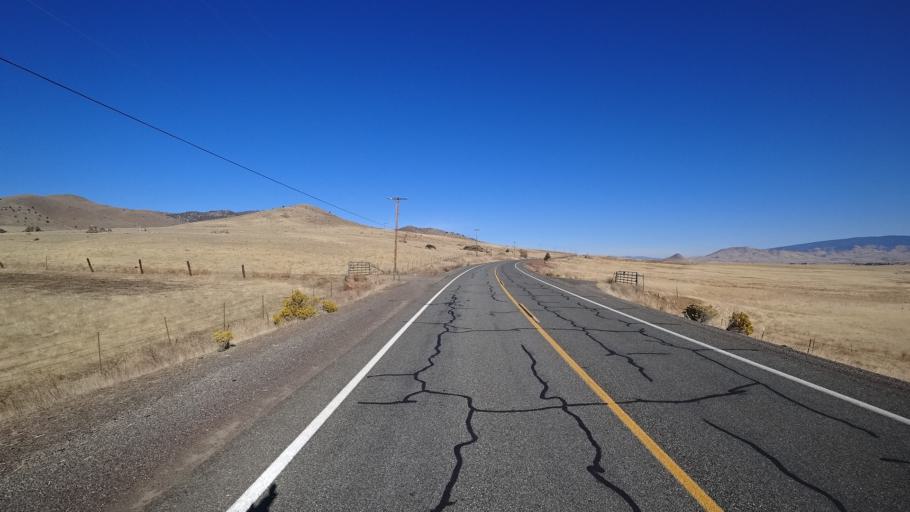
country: US
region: California
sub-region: Siskiyou County
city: Montague
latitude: 41.7747
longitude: -122.5247
